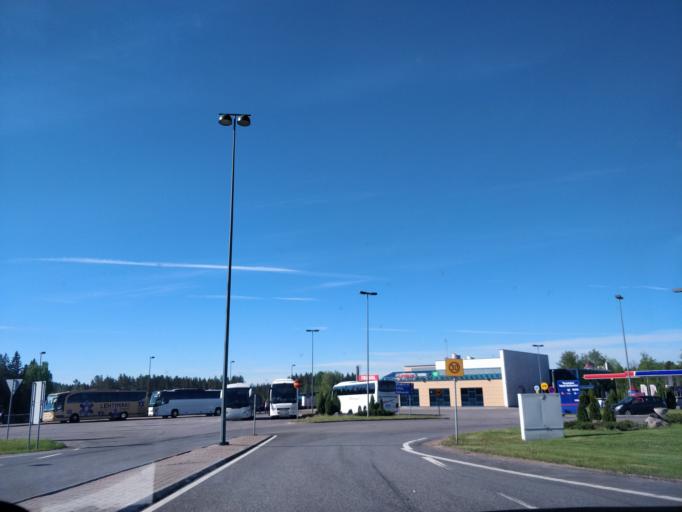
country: FI
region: Varsinais-Suomi
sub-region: Salo
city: Suomusjaervi
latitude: 60.3812
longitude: 23.6171
